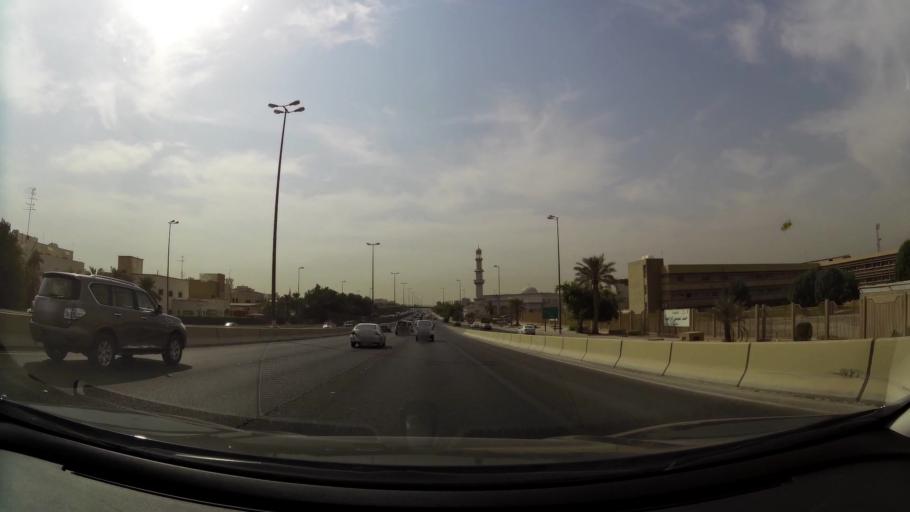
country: KW
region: Al Asimah
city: Ash Shamiyah
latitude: 29.3417
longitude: 47.9720
